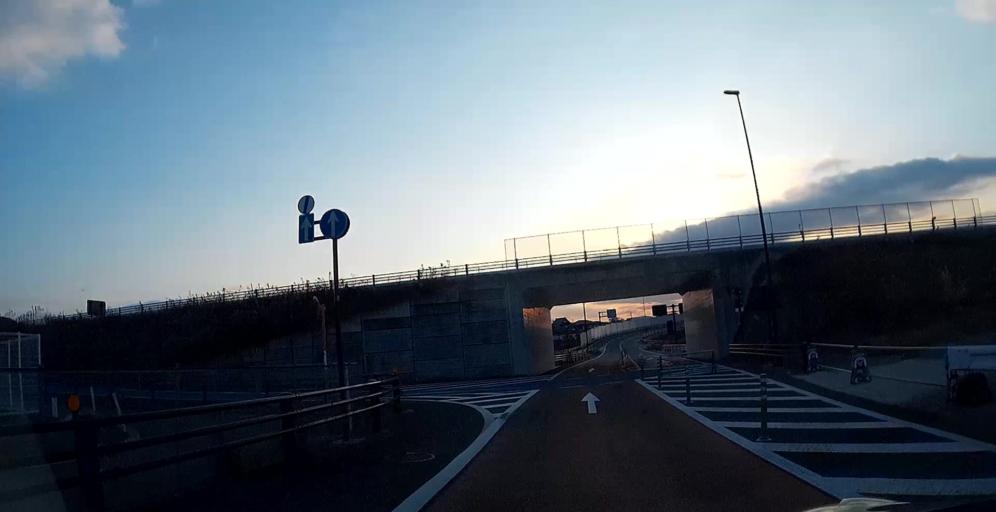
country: JP
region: Kumamoto
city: Kumamoto
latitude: 32.7445
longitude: 130.8037
